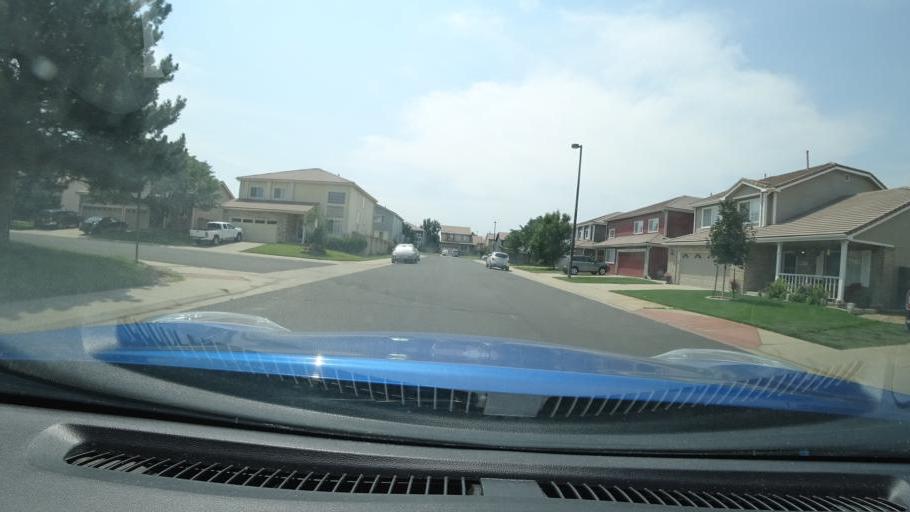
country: US
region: Colorado
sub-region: Adams County
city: Aurora
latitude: 39.7720
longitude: -104.7593
